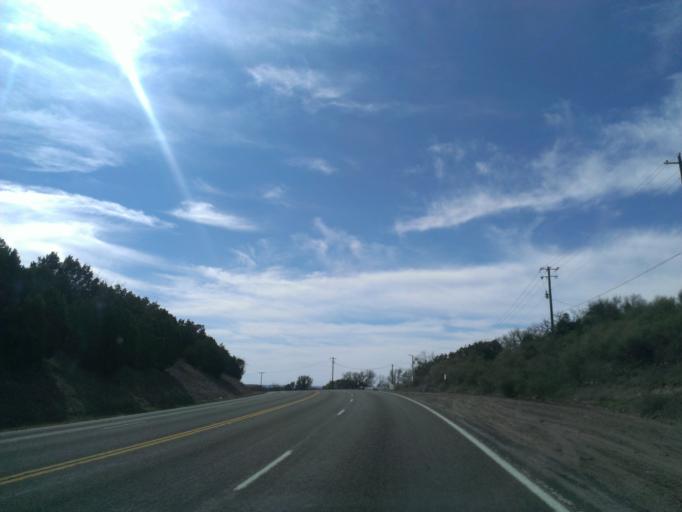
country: US
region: Texas
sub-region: Llano County
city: Kingsland
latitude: 30.6335
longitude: -98.4094
